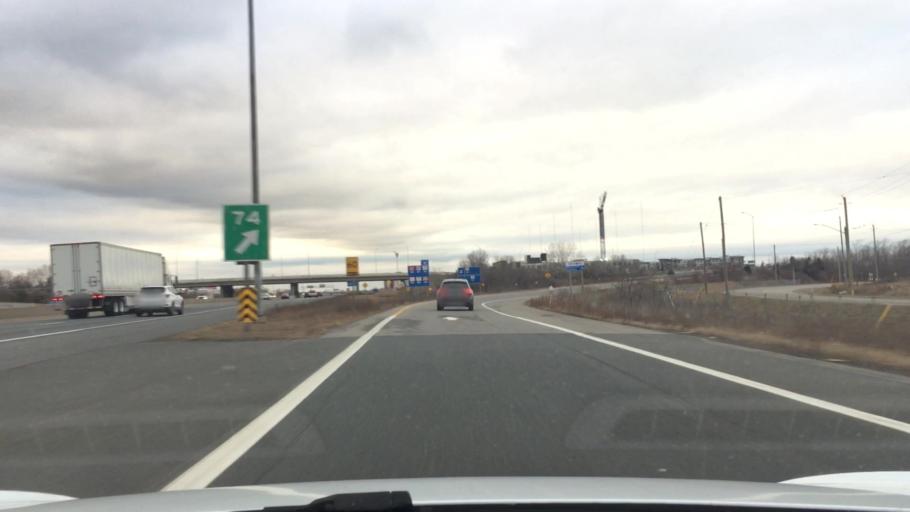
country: CA
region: Ontario
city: Oakville
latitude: 43.2064
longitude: -79.5914
